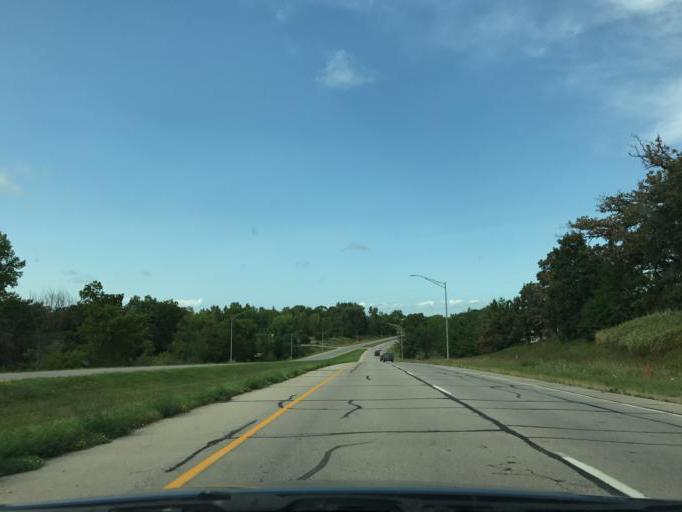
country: US
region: Iowa
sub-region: Jasper County
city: Newton
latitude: 41.6893
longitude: -93.0773
